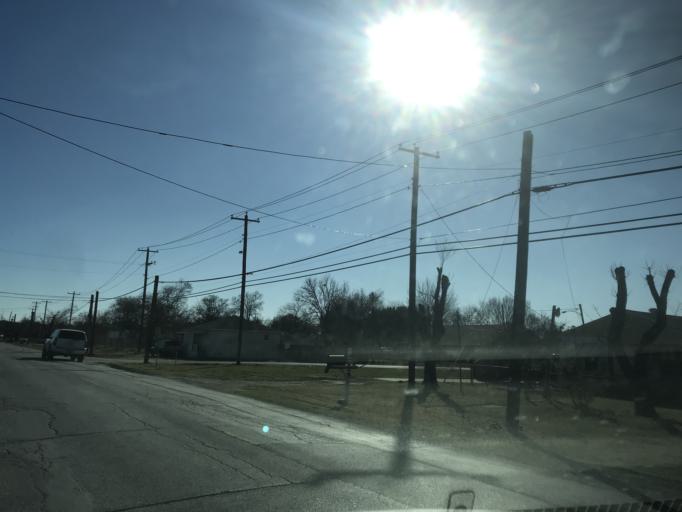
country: US
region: Texas
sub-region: Dallas County
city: Cockrell Hill
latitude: 32.7753
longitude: -96.9047
